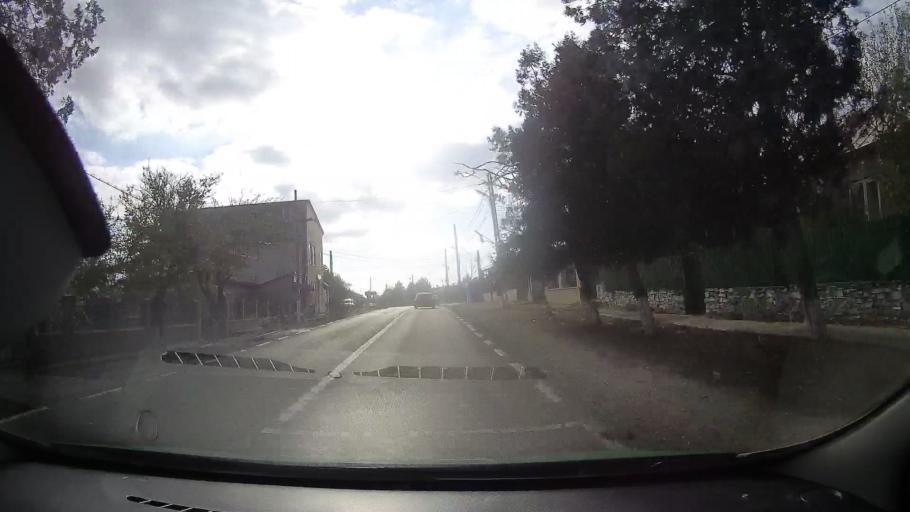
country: RO
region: Tulcea
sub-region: Comuna Topolog
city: Topolog
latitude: 44.8806
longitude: 28.3770
